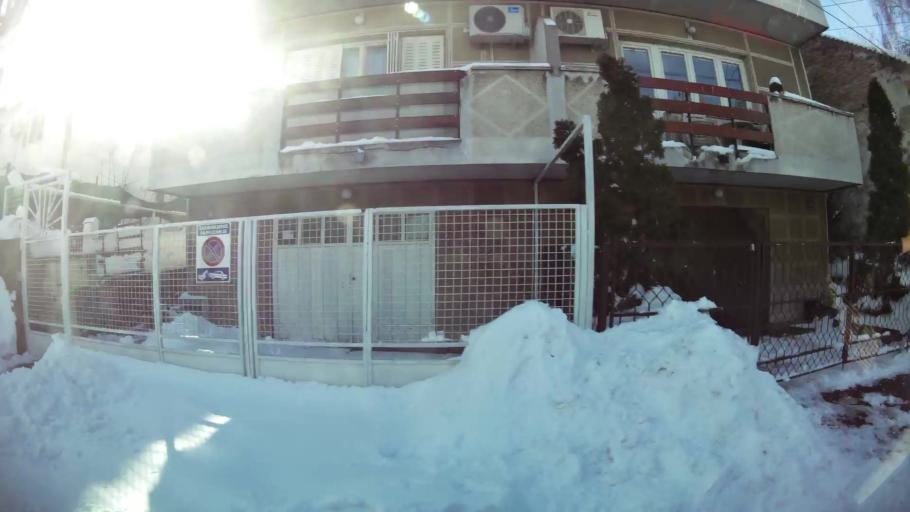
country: RS
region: Central Serbia
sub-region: Belgrade
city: Palilula
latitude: 44.8089
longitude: 20.5146
